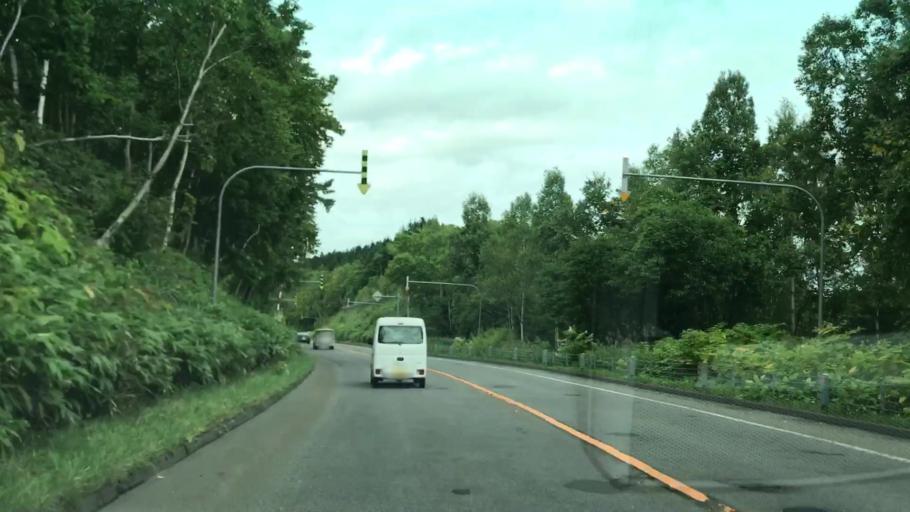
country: JP
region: Hokkaido
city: Niseko Town
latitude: 42.9297
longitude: 140.7140
